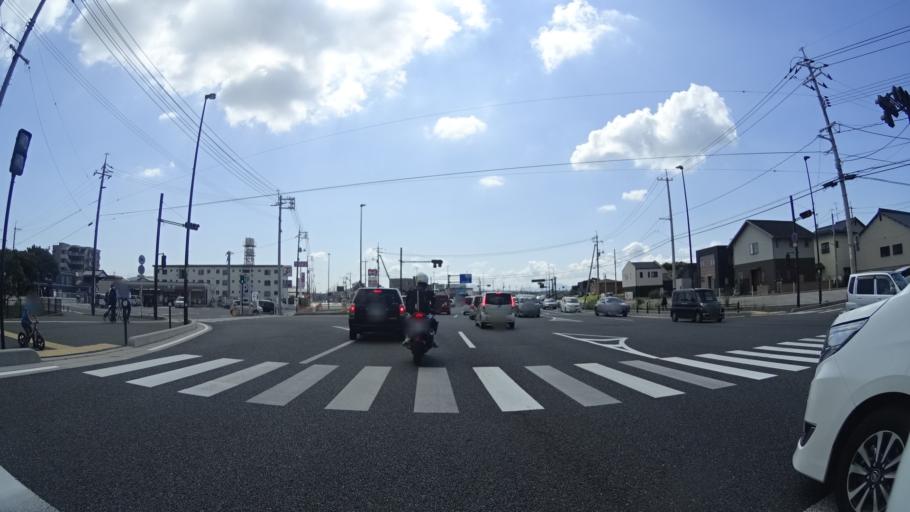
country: JP
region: Yamaguchi
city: Shimonoseki
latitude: 34.0217
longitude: 130.9171
